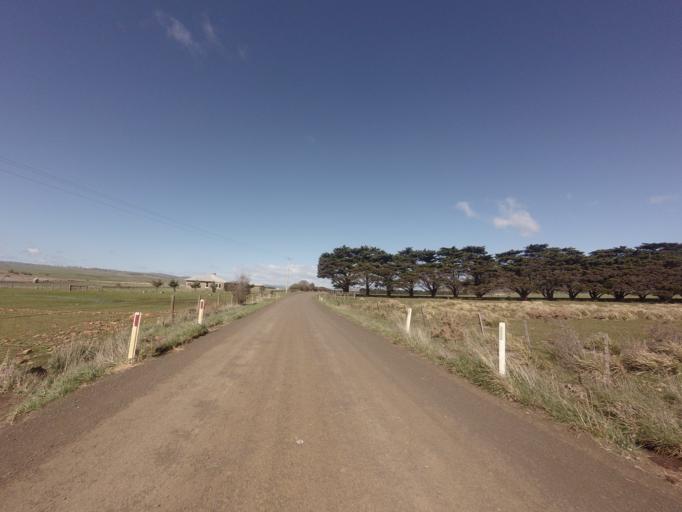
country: AU
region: Tasmania
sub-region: Northern Midlands
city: Evandale
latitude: -41.9497
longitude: 147.4344
